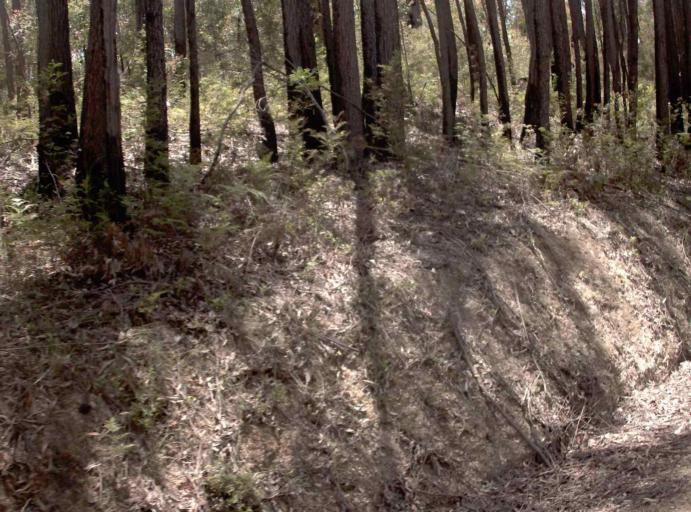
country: AU
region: New South Wales
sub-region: Bombala
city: Bombala
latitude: -37.5739
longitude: 148.9398
